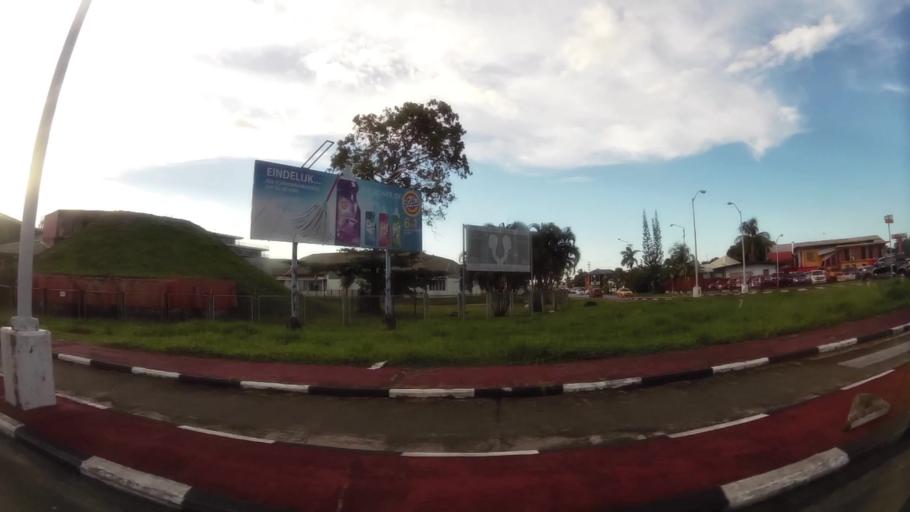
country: SR
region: Paramaribo
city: Paramaribo
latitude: 5.8353
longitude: -55.1819
